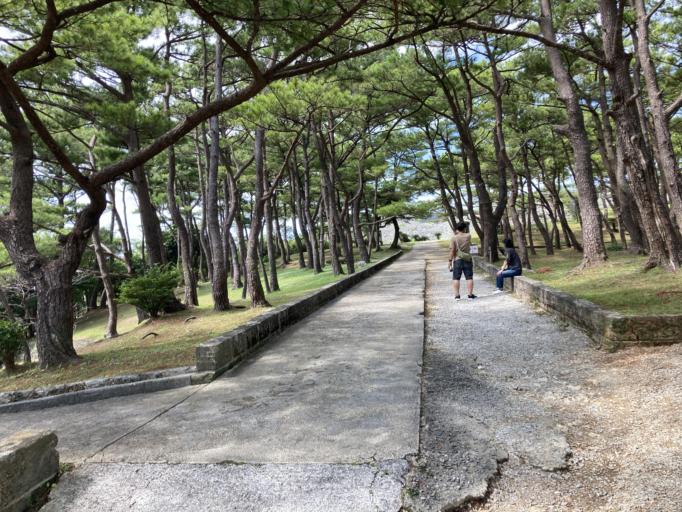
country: JP
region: Okinawa
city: Ishikawa
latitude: 26.4071
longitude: 127.7421
